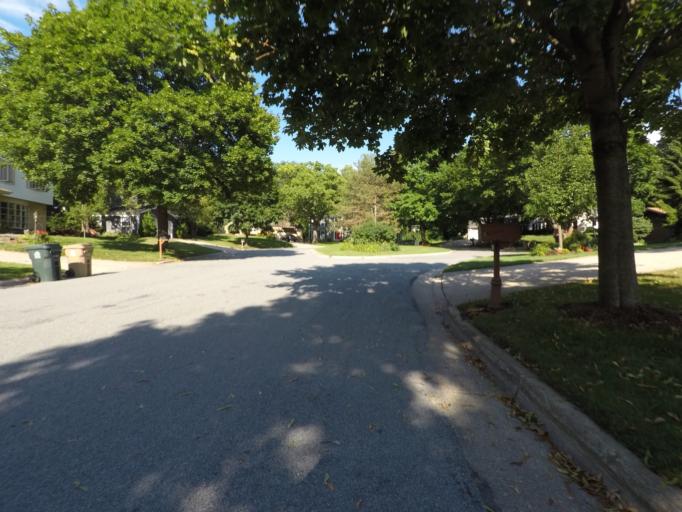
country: US
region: Wisconsin
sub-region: Dane County
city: Middleton
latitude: 43.0728
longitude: -89.5072
